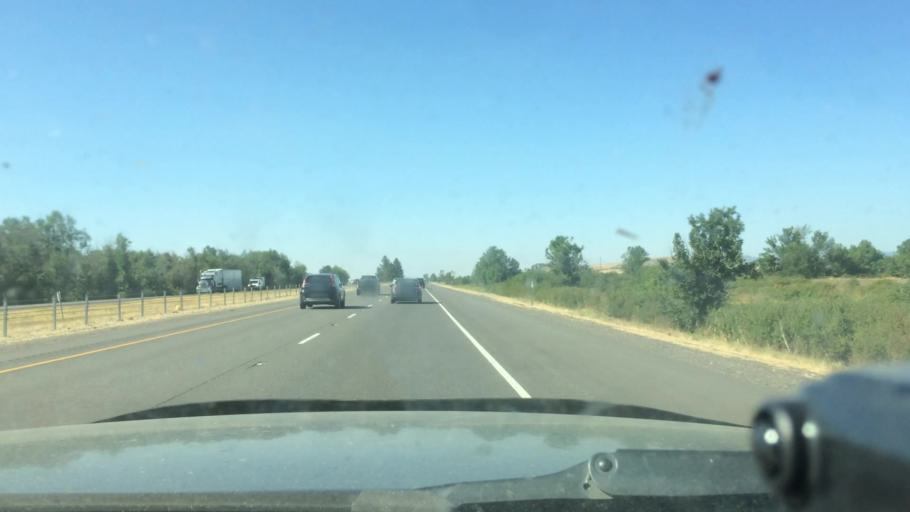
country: US
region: Oregon
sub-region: Linn County
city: Harrisburg
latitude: 44.2944
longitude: -123.0608
